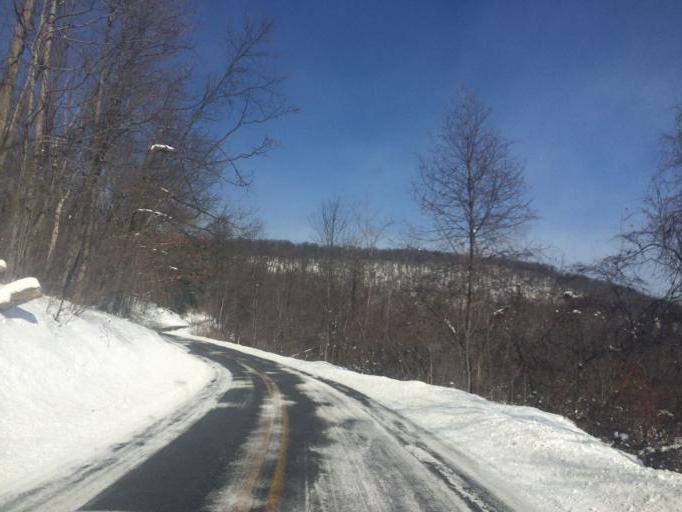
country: US
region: Pennsylvania
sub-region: Centre County
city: Stormstown
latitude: 40.8753
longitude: -78.0183
